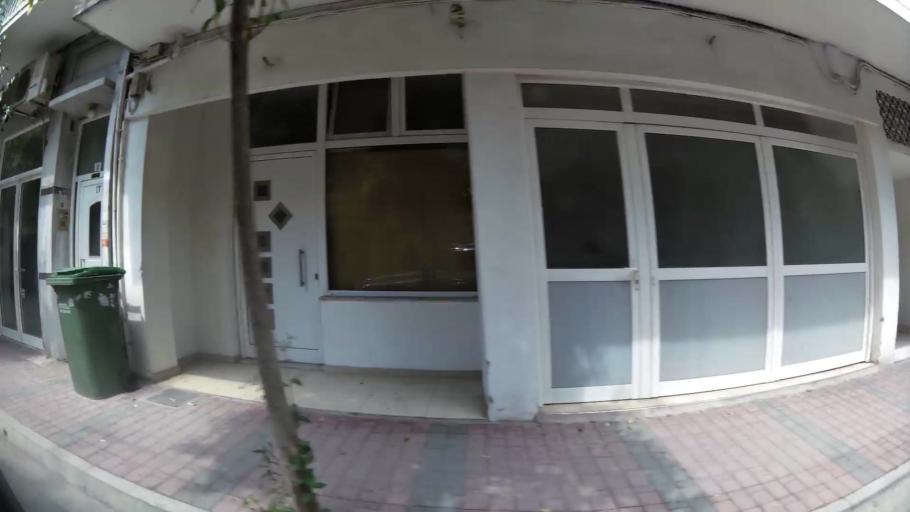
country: GR
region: Central Macedonia
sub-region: Nomos Pierias
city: Katerini
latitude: 40.2717
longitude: 22.5130
